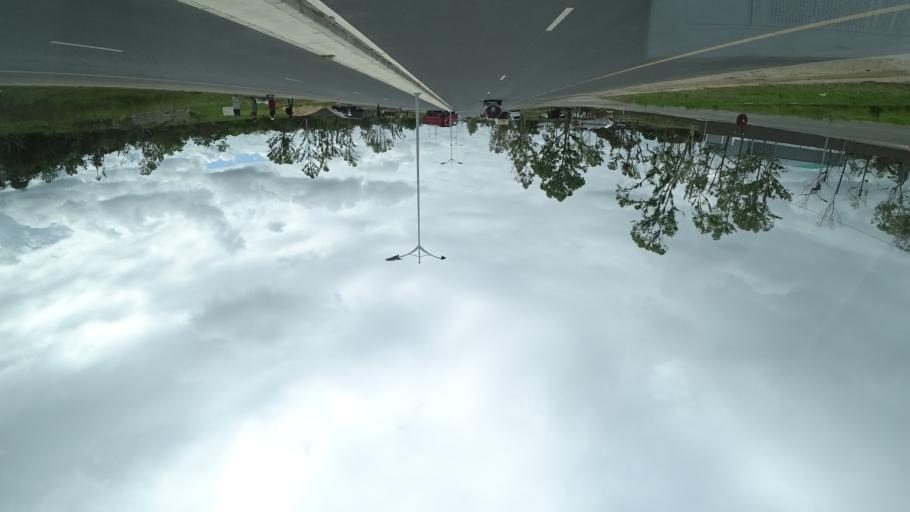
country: MZ
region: Sofala
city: Dondo
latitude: -19.7005
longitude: 34.7862
